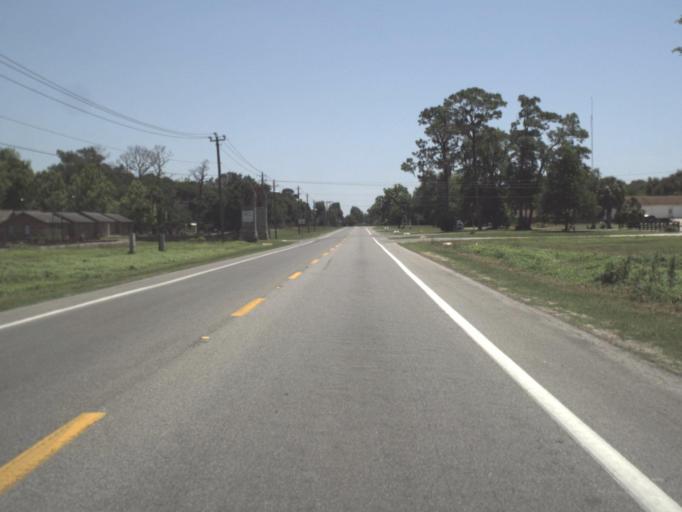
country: US
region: Florida
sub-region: Suwannee County
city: Live Oak
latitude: 30.3072
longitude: -83.0090
